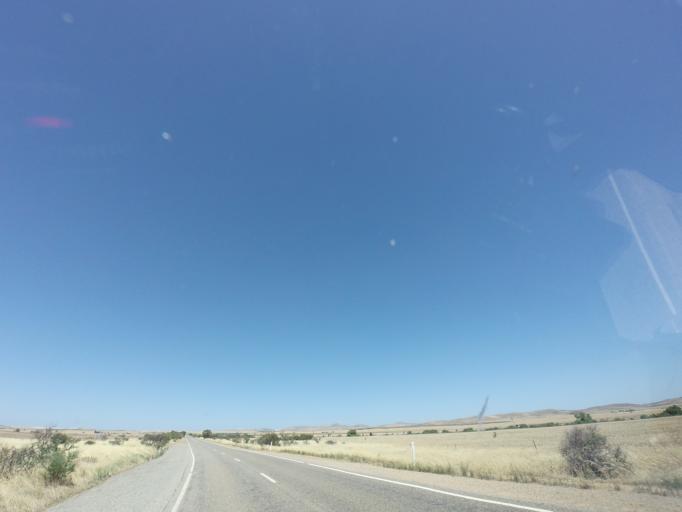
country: AU
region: South Australia
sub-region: Peterborough
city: Peterborough
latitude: -32.7138
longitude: 138.4530
